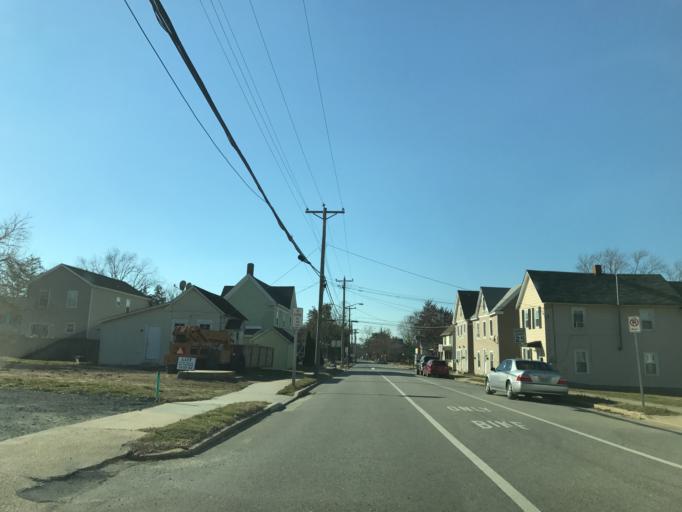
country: US
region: Maryland
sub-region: Caroline County
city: Denton
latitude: 38.8865
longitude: -75.8293
